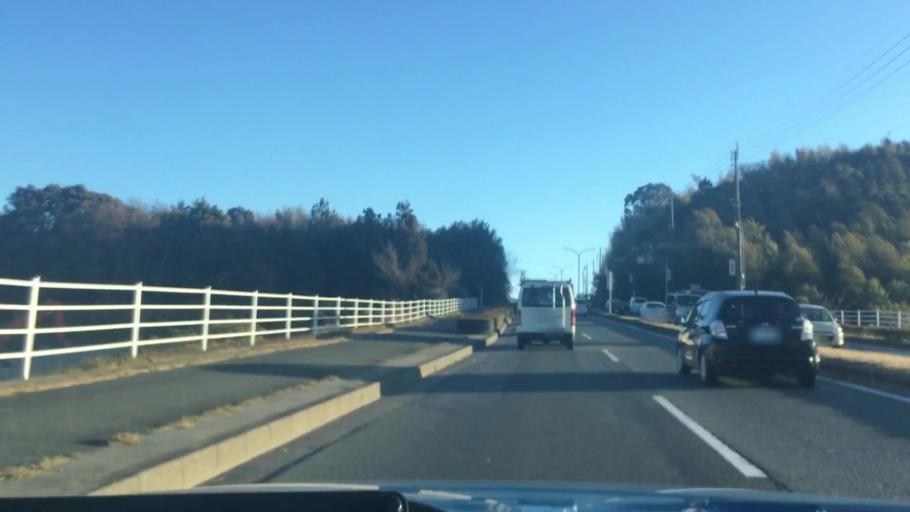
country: JP
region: Shizuoka
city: Hamamatsu
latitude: 34.7451
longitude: 137.6658
